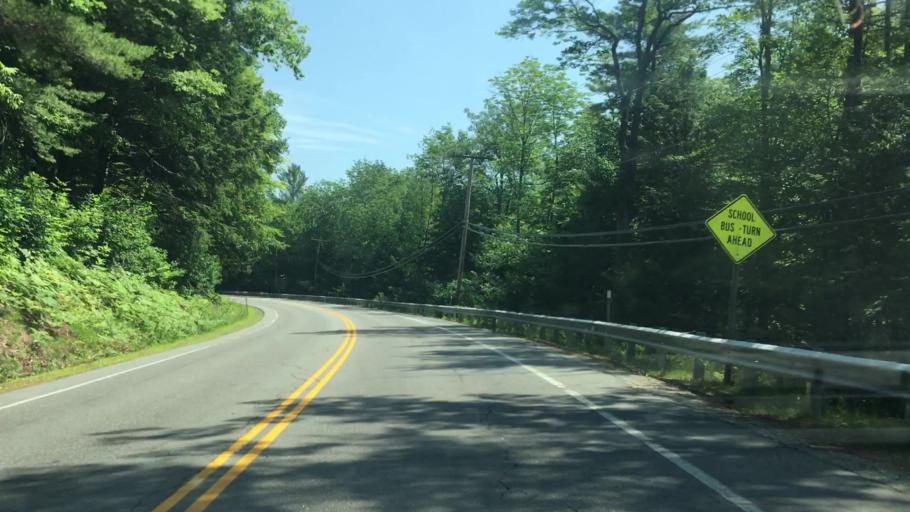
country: US
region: New Hampshire
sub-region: Sullivan County
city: Newport
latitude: 43.4161
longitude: -72.1799
